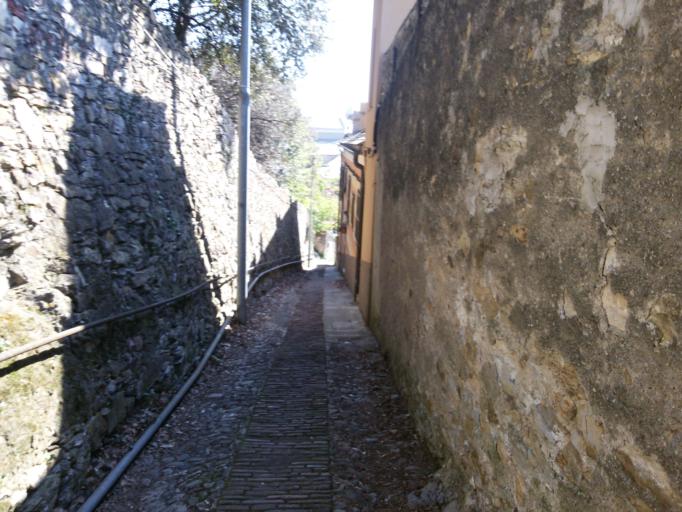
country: IT
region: Liguria
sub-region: Provincia di Genova
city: Genoa
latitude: 44.4140
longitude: 8.9641
